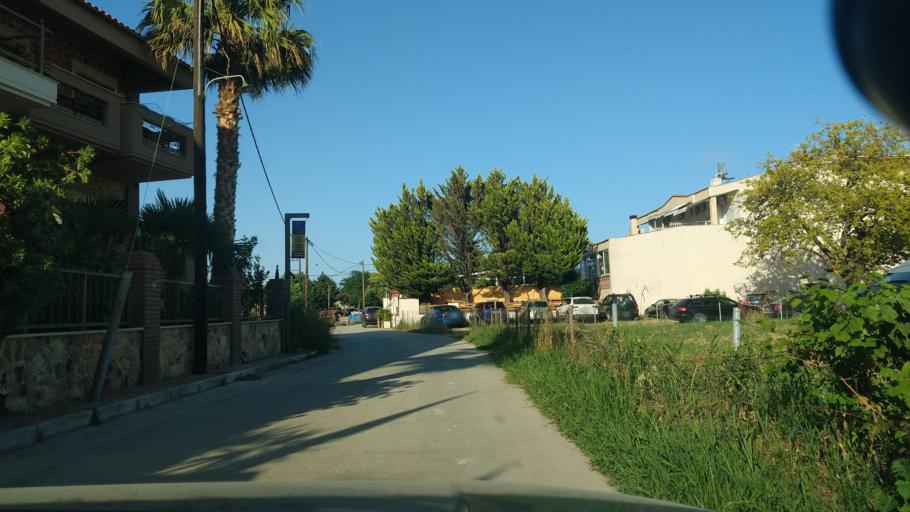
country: GR
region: East Macedonia and Thrace
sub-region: Nomos Kavalas
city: Potamia
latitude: 40.7186
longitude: 24.7543
